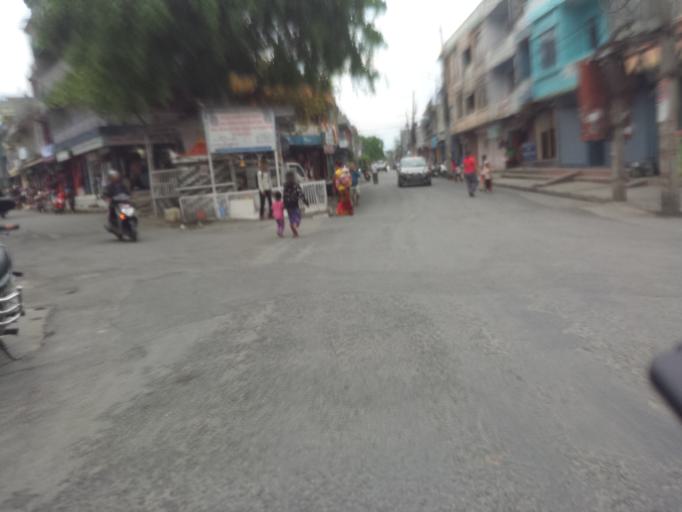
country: NP
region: Western Region
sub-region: Gandaki Zone
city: Pokhara
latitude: 28.2009
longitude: 83.9970
